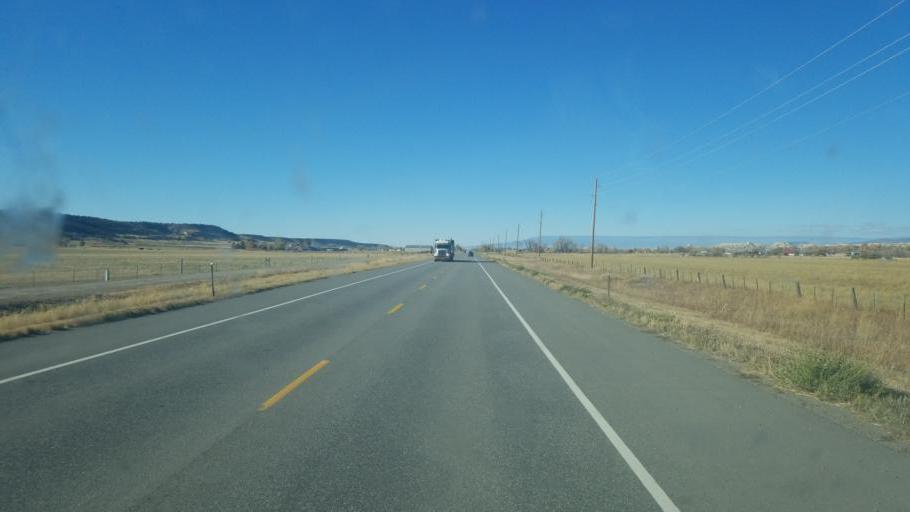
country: US
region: Colorado
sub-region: Montrose County
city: Montrose
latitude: 38.3492
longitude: -107.7938
